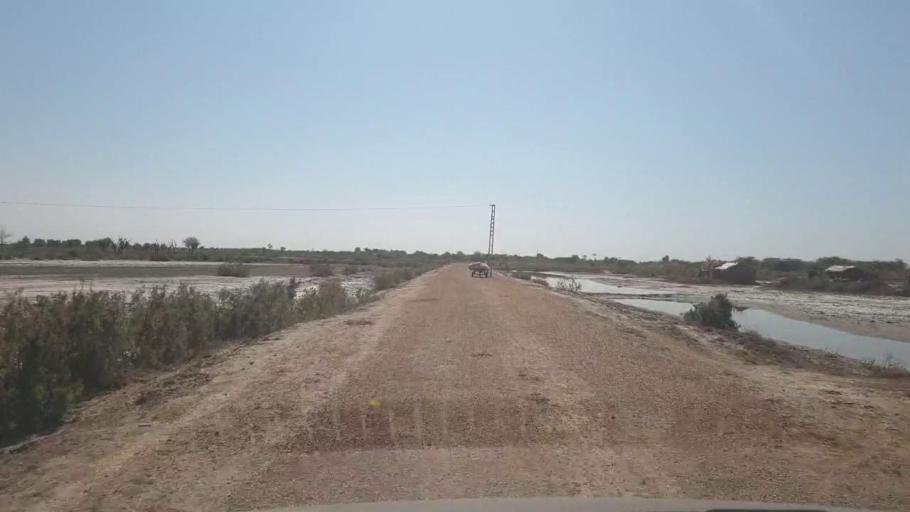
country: PK
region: Sindh
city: Dhoro Naro
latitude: 25.4457
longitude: 69.6112
